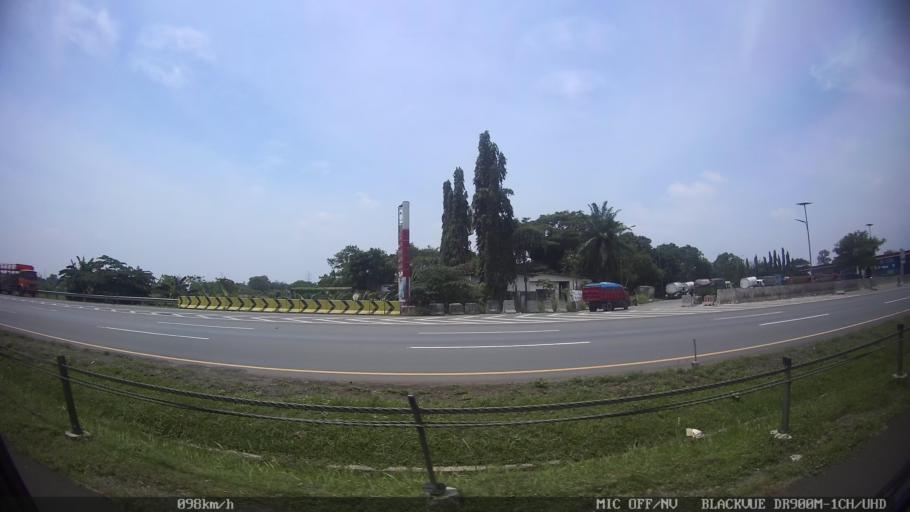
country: ID
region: West Java
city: Kresek
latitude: -6.1856
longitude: 106.4071
